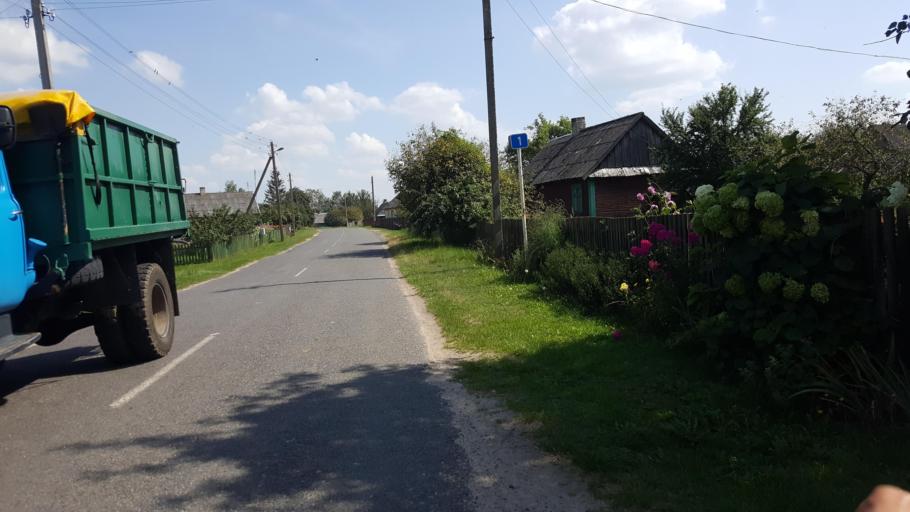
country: PL
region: Podlasie
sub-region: Powiat hajnowski
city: Czeremcha
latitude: 52.5123
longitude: 23.5489
